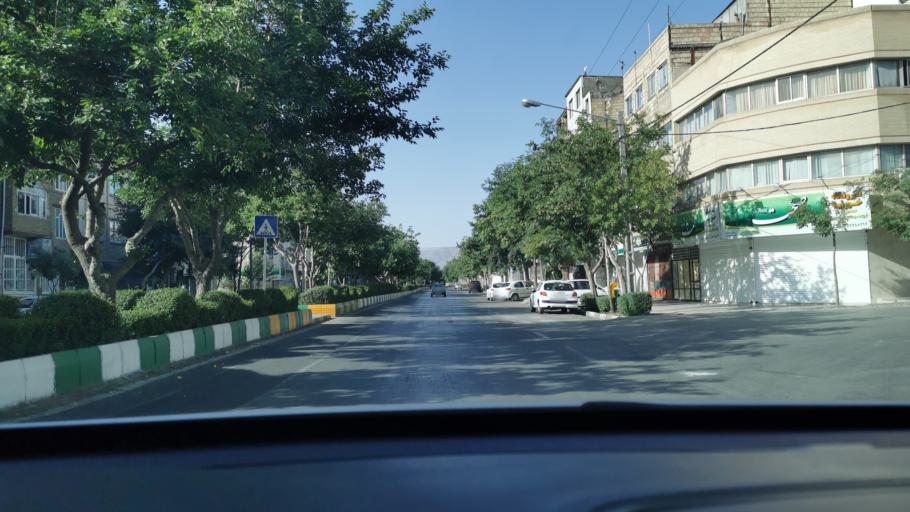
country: IR
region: Razavi Khorasan
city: Mashhad
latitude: 36.3401
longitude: 59.5137
